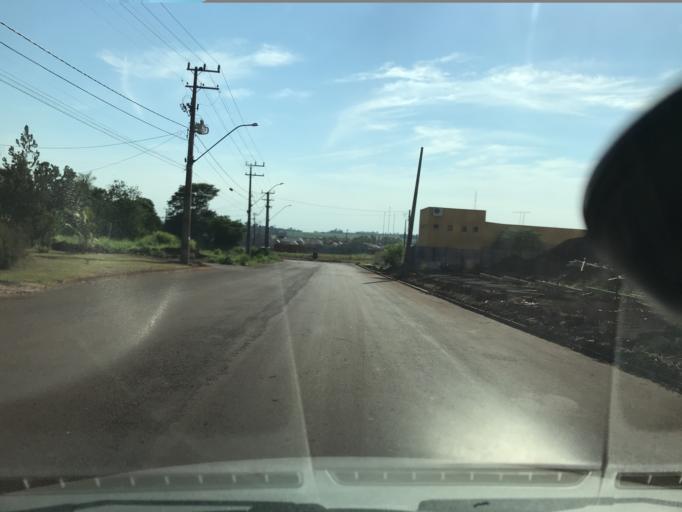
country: BR
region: Parana
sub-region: Palotina
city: Palotina
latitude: -24.2948
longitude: -53.8310
